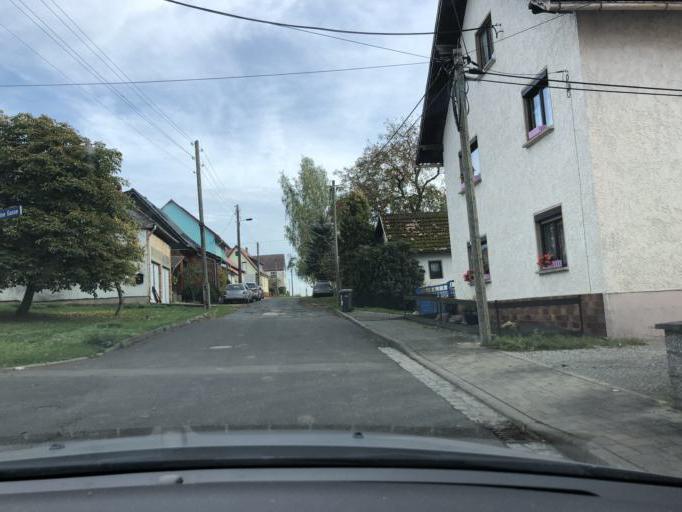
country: DE
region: Thuringia
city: Reurieth
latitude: 50.4189
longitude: 10.6691
